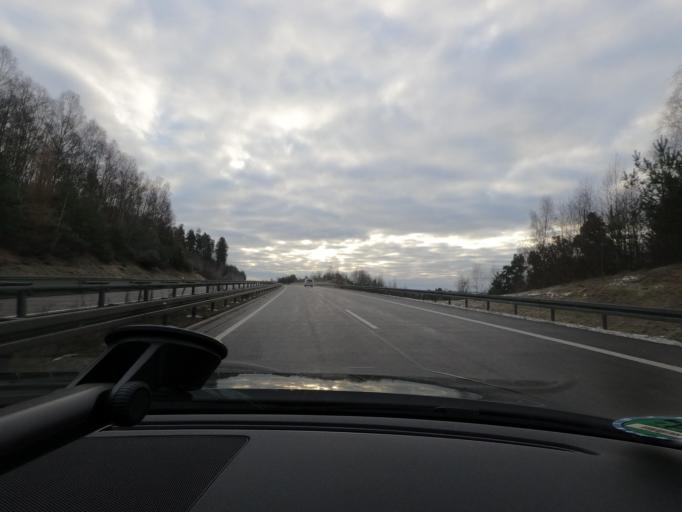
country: DE
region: Thuringia
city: Schleusingen
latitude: 50.5040
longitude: 10.7823
